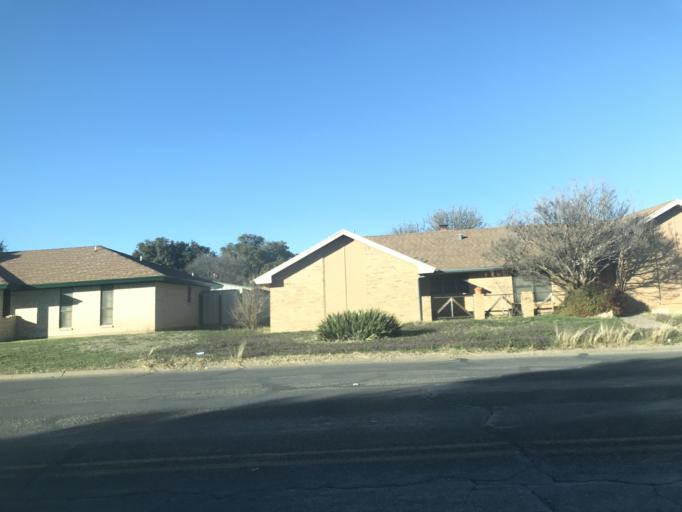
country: US
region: Texas
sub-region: Tom Green County
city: San Angelo
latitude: 31.4273
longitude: -100.4922
